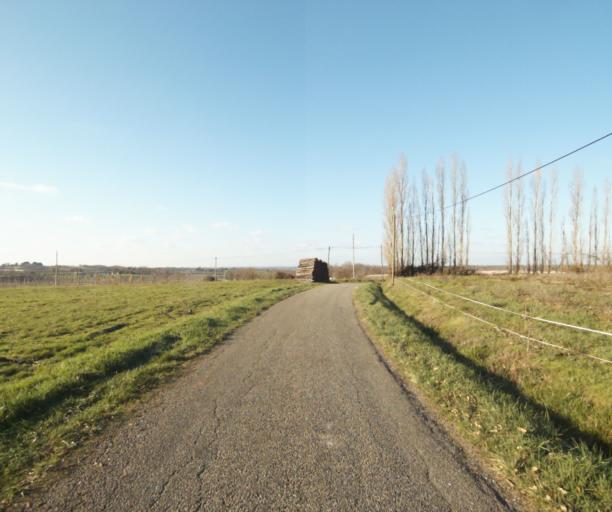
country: FR
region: Midi-Pyrenees
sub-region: Departement du Tarn-et-Garonne
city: Moissac
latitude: 44.1461
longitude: 1.0616
